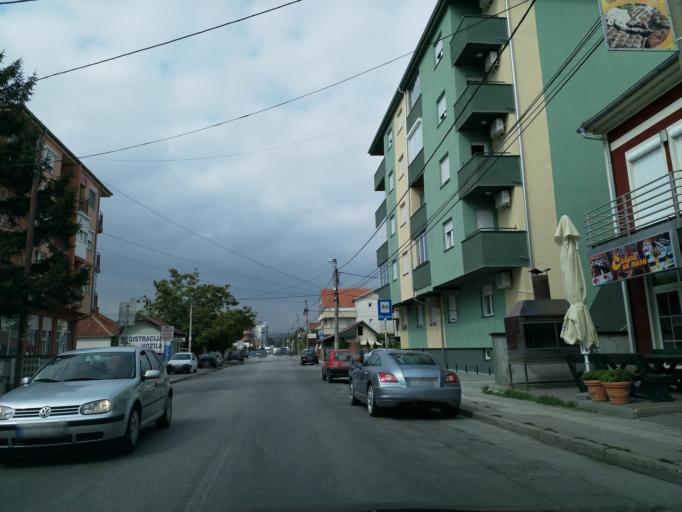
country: RS
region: Central Serbia
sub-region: Pomoravski Okrug
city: Jagodina
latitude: 43.9845
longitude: 21.2548
